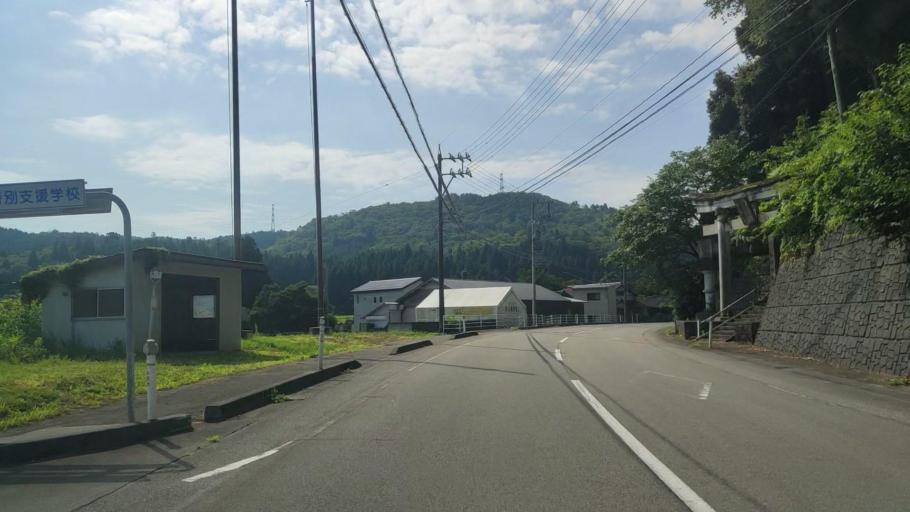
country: JP
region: Ishikawa
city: Komatsu
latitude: 36.3560
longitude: 136.5044
